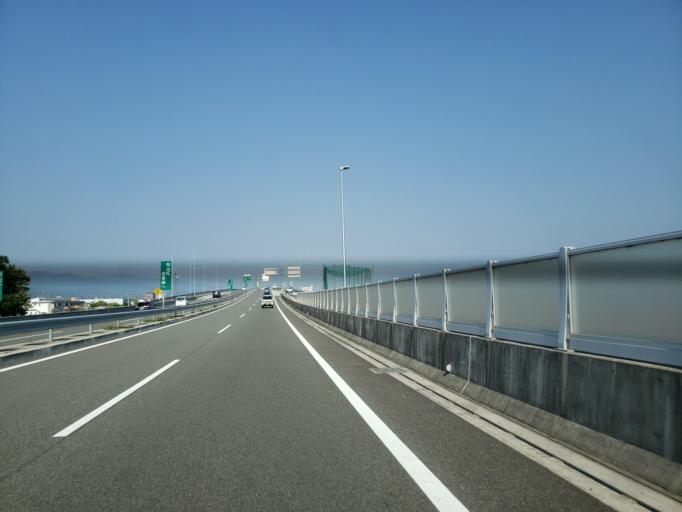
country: JP
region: Ehime
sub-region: Shikoku-chuo Shi
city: Matsuyama
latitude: 33.8023
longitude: 132.7687
